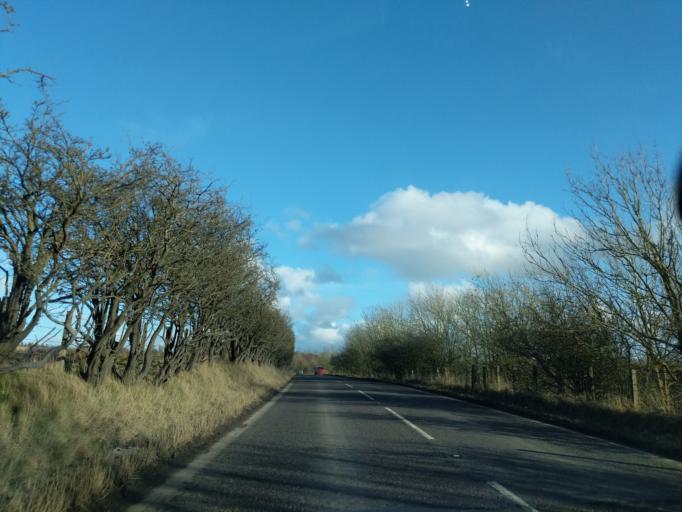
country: GB
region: Scotland
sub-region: North Lanarkshire
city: Shotts
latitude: 55.8082
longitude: -3.7889
